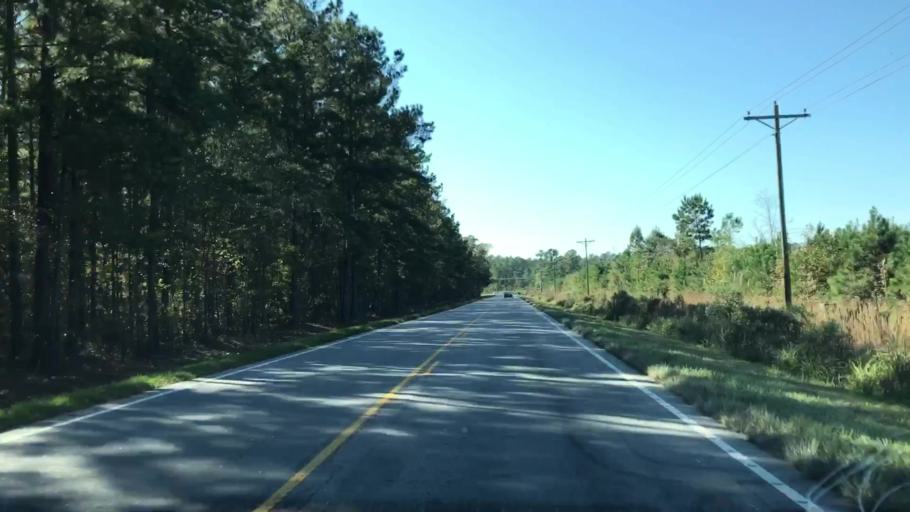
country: US
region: South Carolina
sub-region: Jasper County
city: Ridgeland
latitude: 32.4117
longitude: -80.9019
